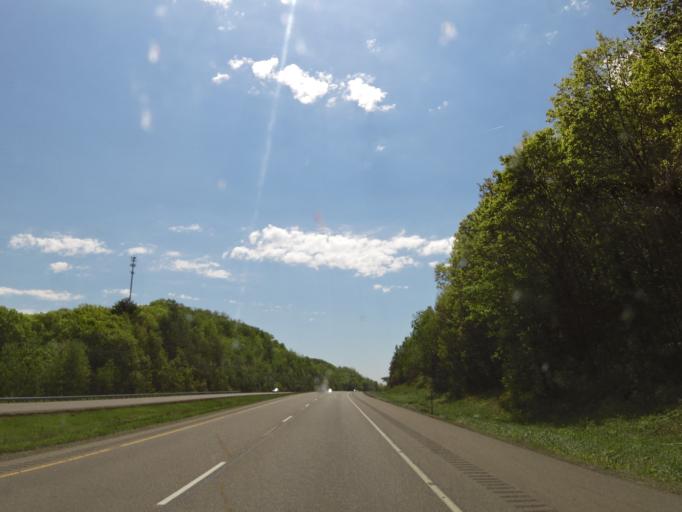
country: US
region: Wisconsin
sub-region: Trempealeau County
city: Osseo
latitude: 44.4387
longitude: -91.0736
